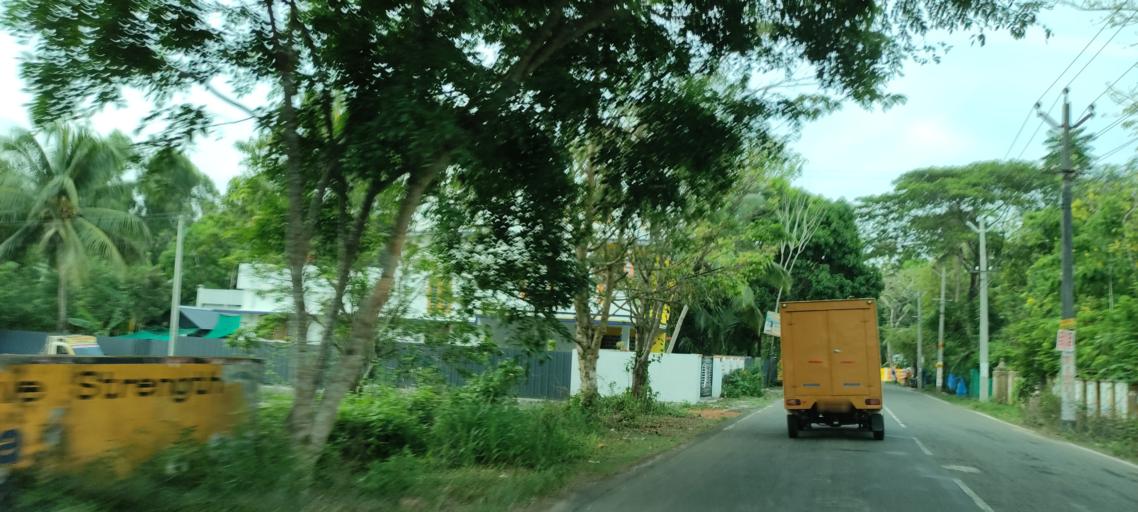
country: IN
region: Kerala
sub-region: Kottayam
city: Vaikam
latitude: 9.7588
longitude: 76.3626
